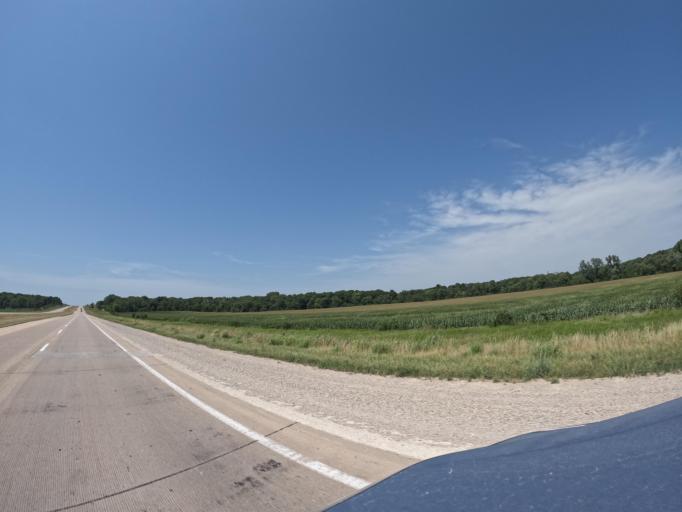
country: US
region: Iowa
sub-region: Henry County
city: Mount Pleasant
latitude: 40.9716
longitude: -91.6461
